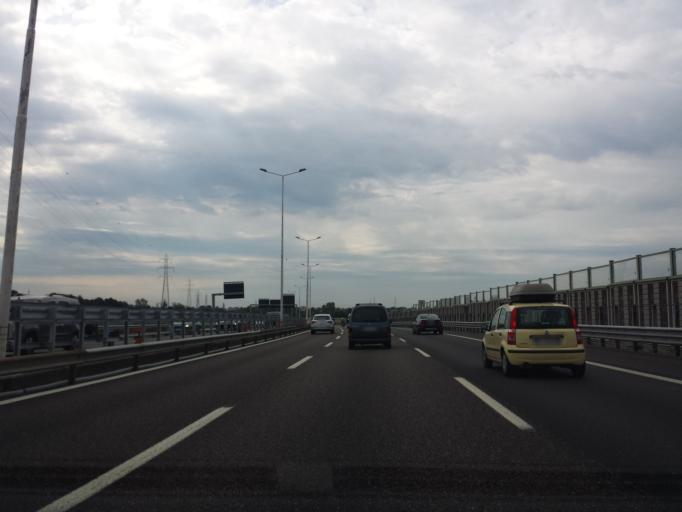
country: IT
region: Lombardy
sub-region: Citta metropolitana di Milano
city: Figino
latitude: 45.4876
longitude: 9.0673
